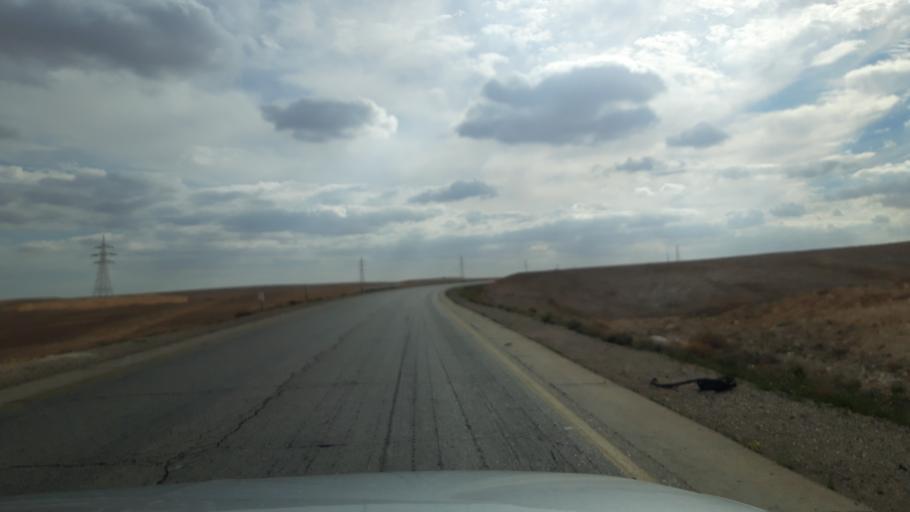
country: JO
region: Amman
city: Al Azraq ash Shamali
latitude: 31.7447
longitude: 36.5361
